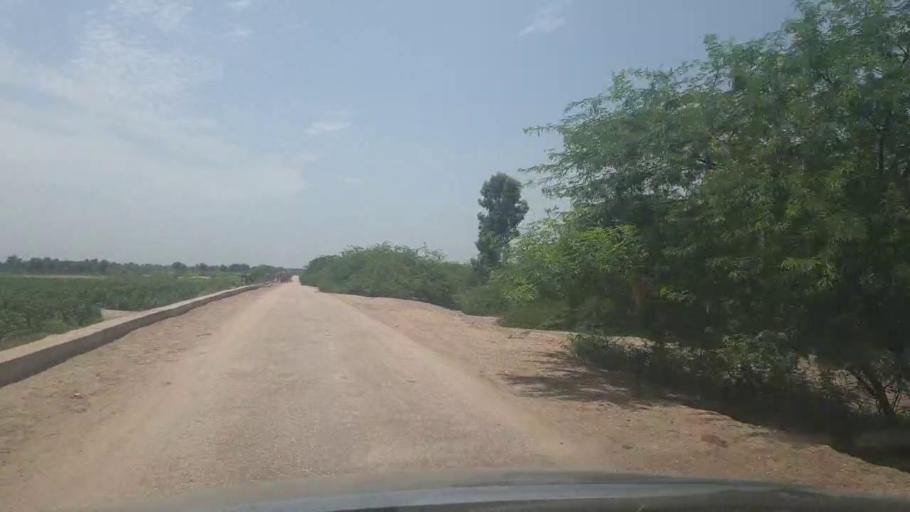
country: PK
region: Sindh
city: Kot Diji
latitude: 27.4087
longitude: 68.7318
